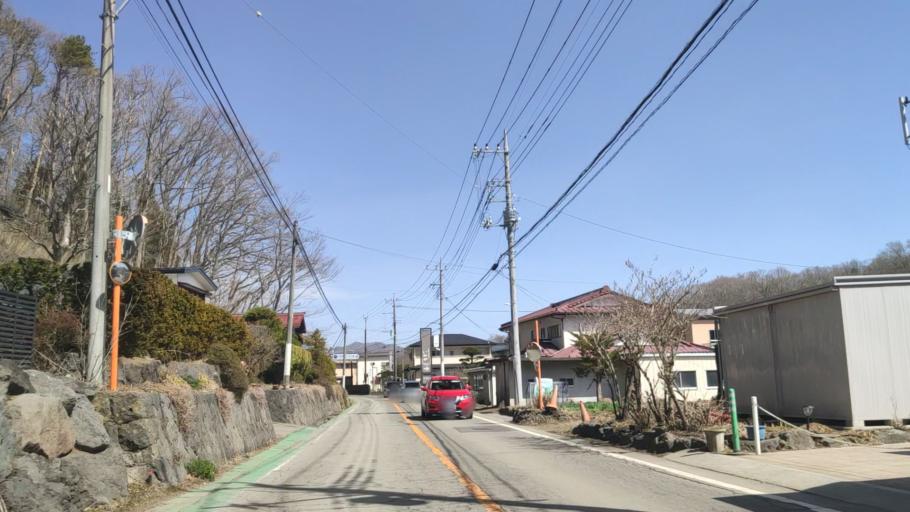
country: JP
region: Yamanashi
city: Fujikawaguchiko
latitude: 35.4570
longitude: 138.8236
